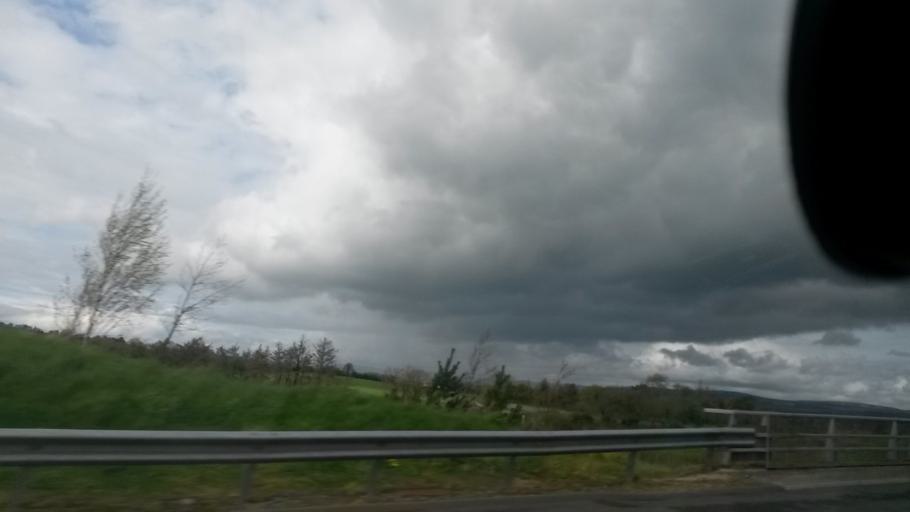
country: IE
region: Leinster
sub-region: Laois
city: Mountrath
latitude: 52.9750
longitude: -7.4331
